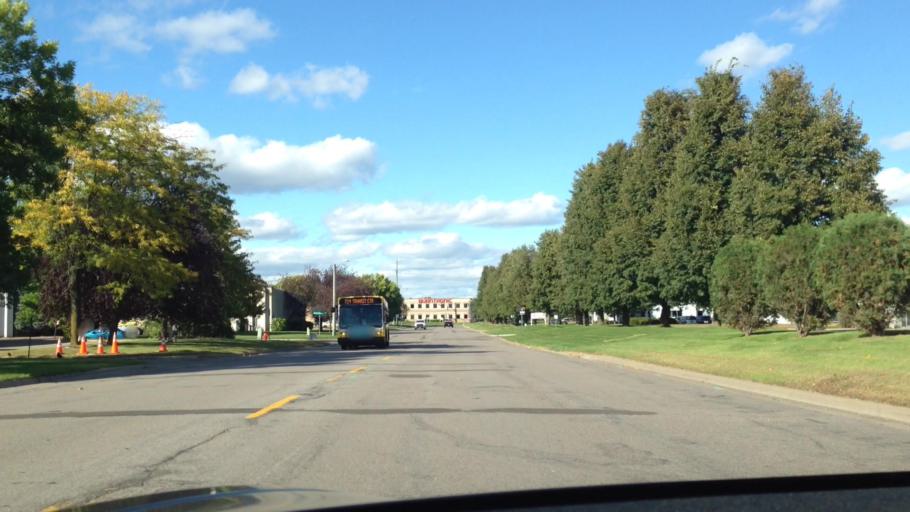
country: US
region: Minnesota
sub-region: Hennepin County
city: Osseo
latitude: 45.1135
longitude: -93.3869
